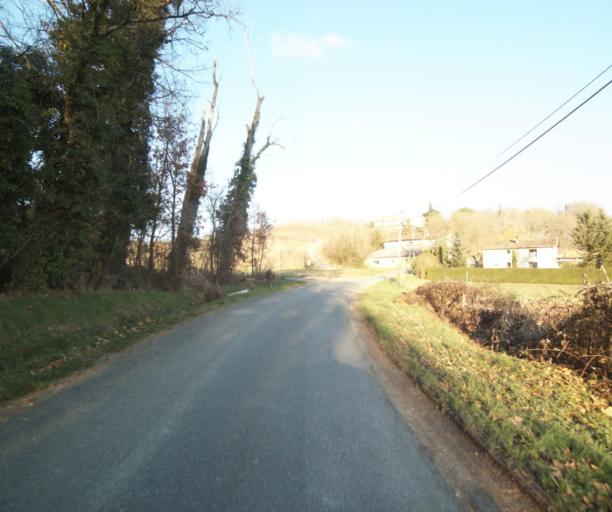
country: FR
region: Midi-Pyrenees
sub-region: Departement du Tarn-et-Garonne
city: Moissac
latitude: 44.1236
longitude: 1.1310
